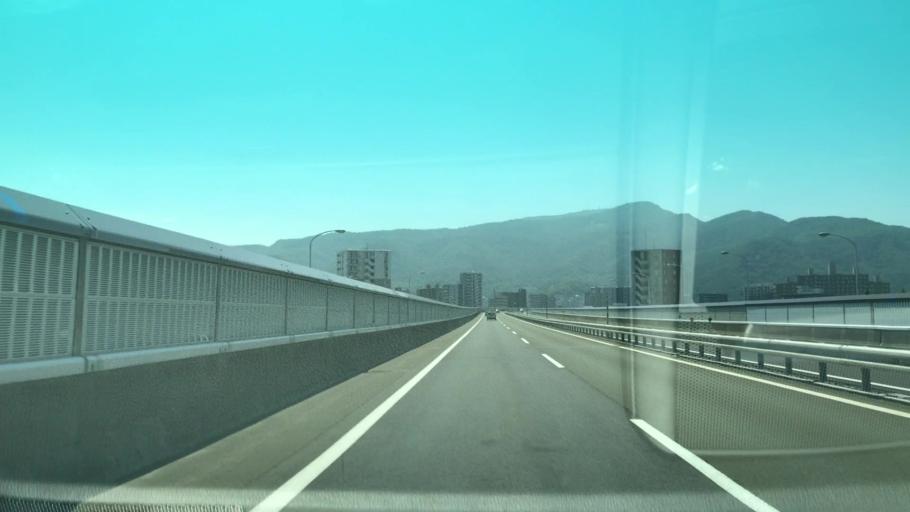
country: JP
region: Hokkaido
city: Sapporo
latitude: 43.0946
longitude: 141.2891
